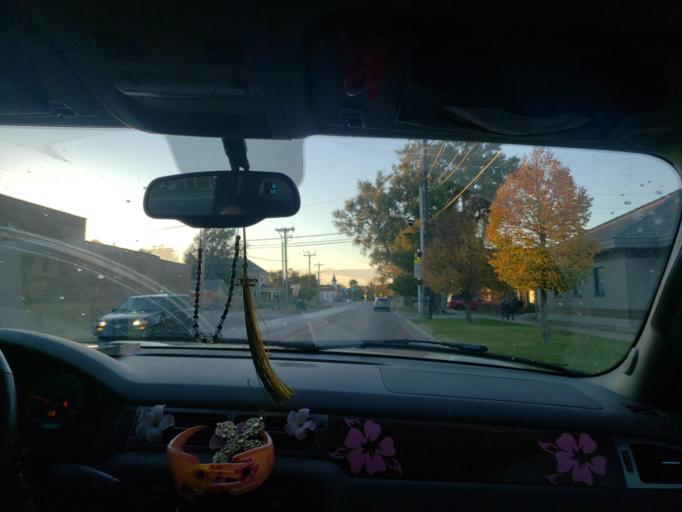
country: US
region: Kansas
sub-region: Finney County
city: Garden City
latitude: 37.9718
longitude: -100.8727
